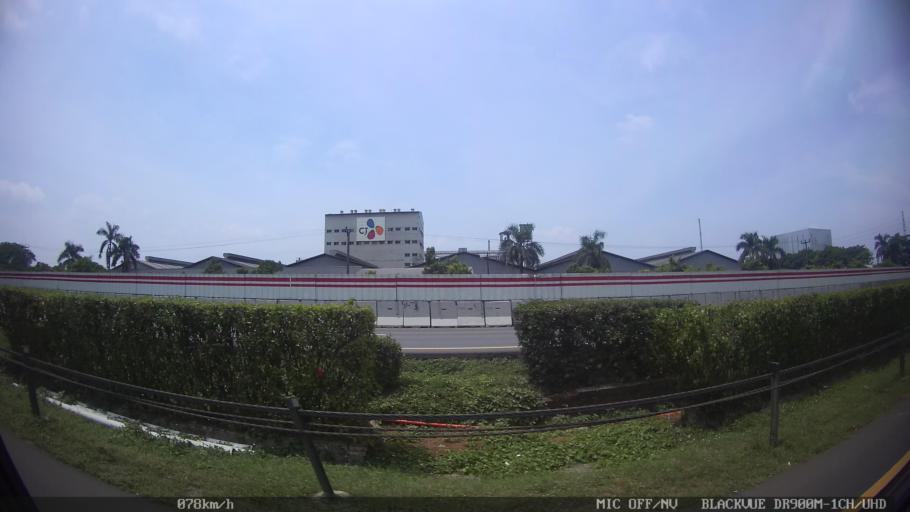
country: ID
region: West Java
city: Kresek
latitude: -6.1687
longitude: 106.3404
